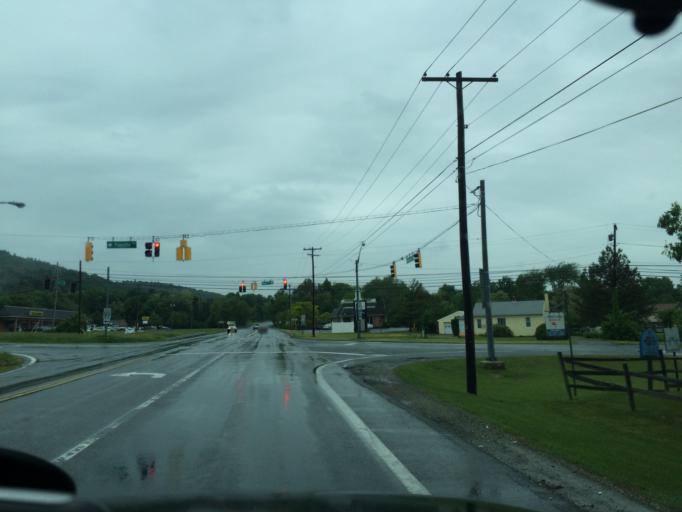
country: US
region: Maryland
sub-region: Washington County
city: Smithsburg
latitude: 39.6495
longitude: -77.5681
